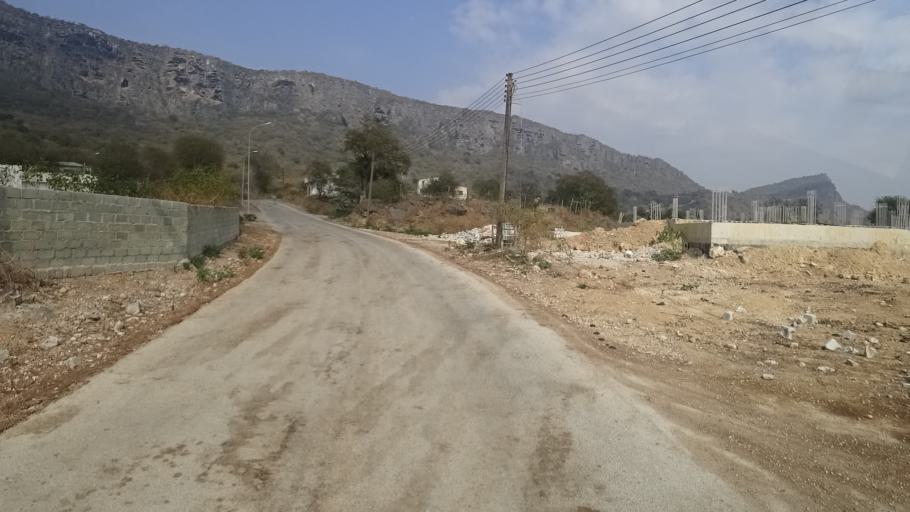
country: YE
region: Al Mahrah
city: Hawf
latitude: 16.7143
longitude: 53.2523
